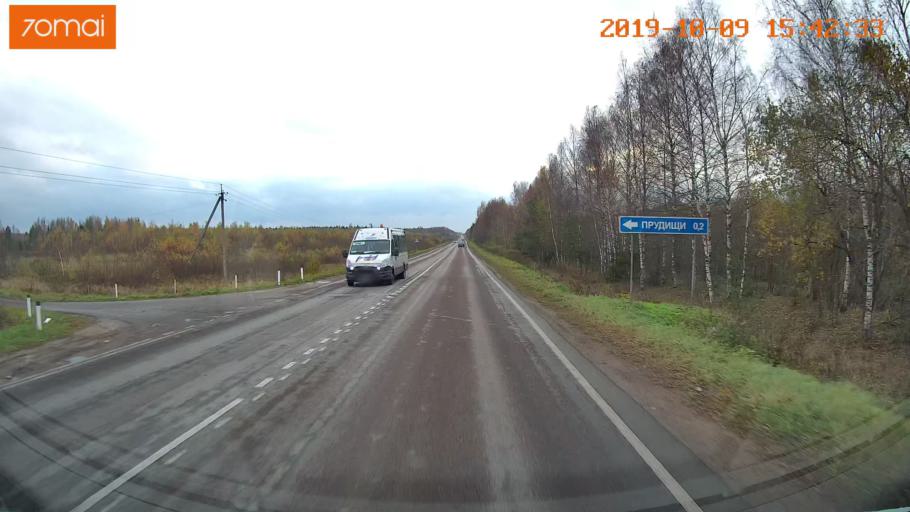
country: RU
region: Kostroma
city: Oktyabr'skiy
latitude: 57.8671
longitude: 41.1047
